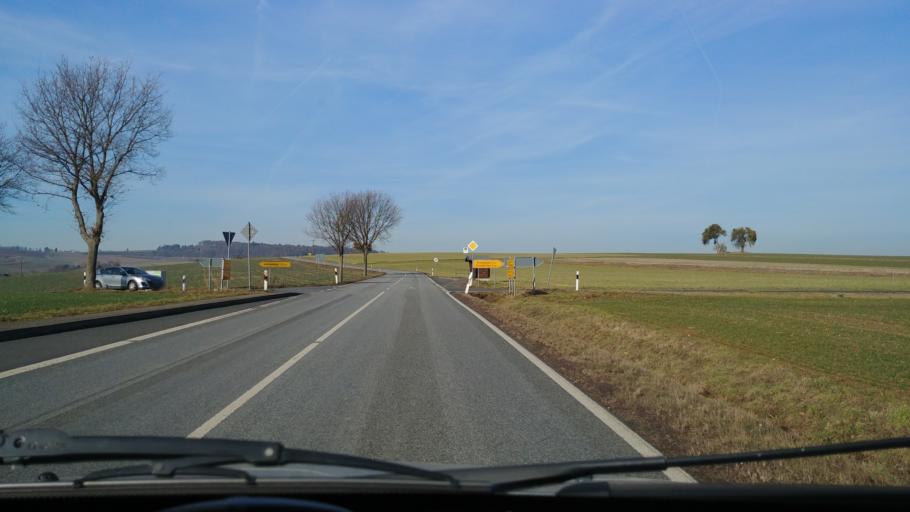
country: DE
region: Rheinland-Pfalz
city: Niederbachheim
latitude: 50.2495
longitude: 7.7710
